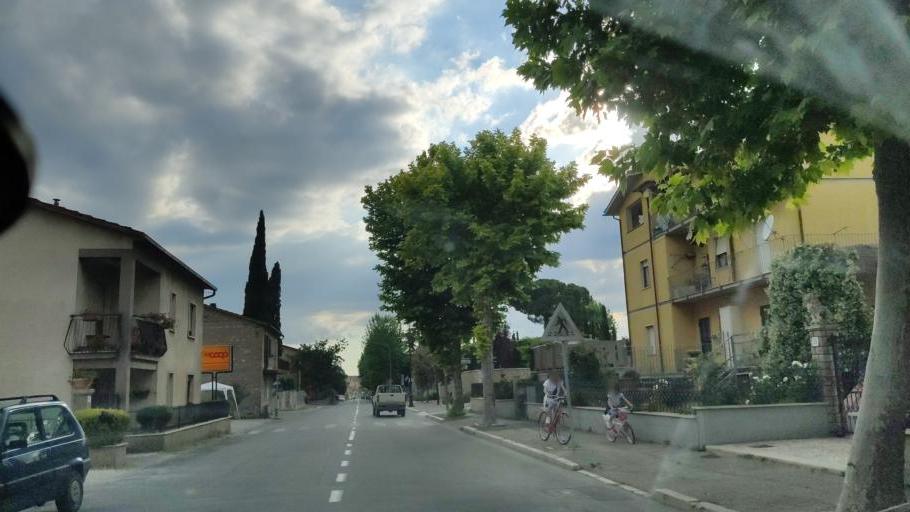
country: IT
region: Umbria
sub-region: Provincia di Terni
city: Giove
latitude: 42.5105
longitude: 12.3331
